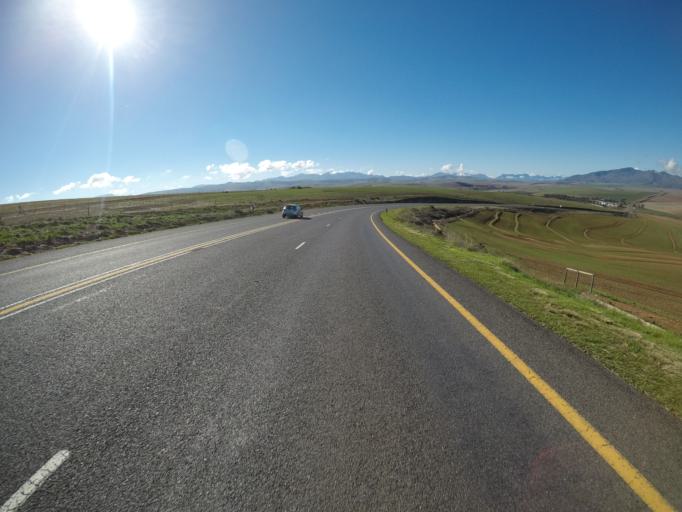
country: ZA
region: Western Cape
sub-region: Overberg District Municipality
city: Caledon
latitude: -34.2133
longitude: 19.3212
